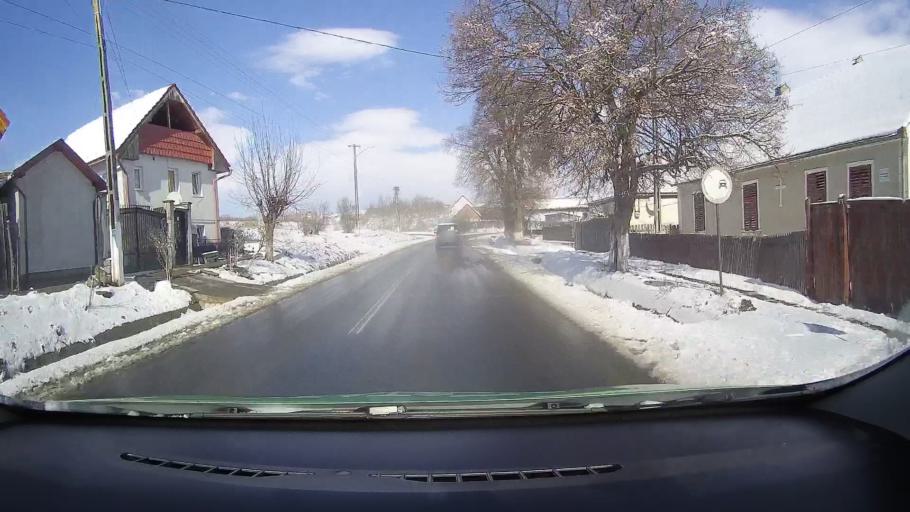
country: RO
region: Sibiu
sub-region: Comuna Nocrich
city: Nocrich
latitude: 45.9008
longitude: 24.4592
